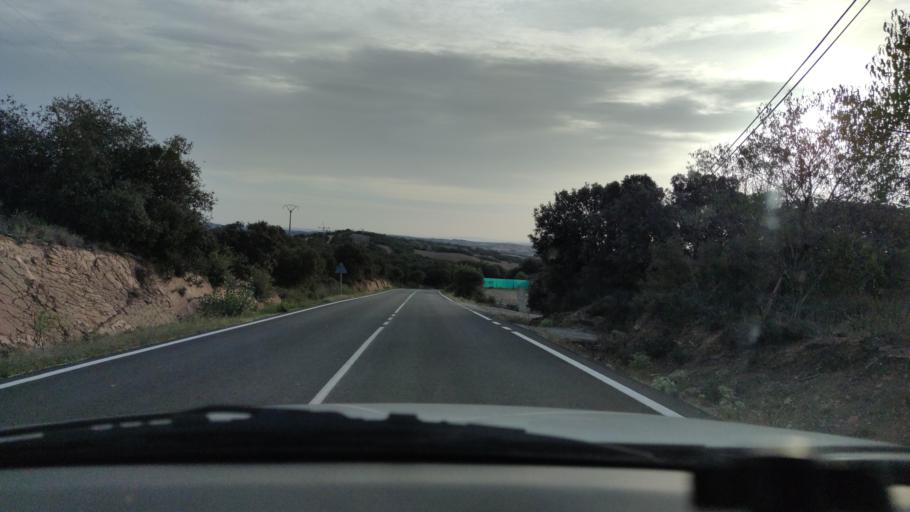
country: ES
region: Catalonia
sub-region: Provincia de Lleida
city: Artesa de Segre
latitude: 41.8479
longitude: 1.0534
